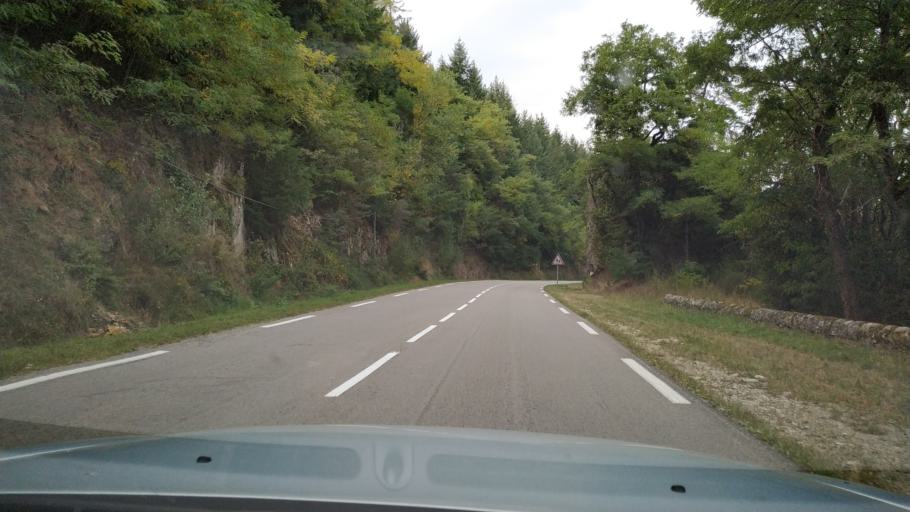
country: FR
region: Rhone-Alpes
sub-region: Departement de l'Ardeche
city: Desaignes
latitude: 44.9884
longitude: 4.5299
